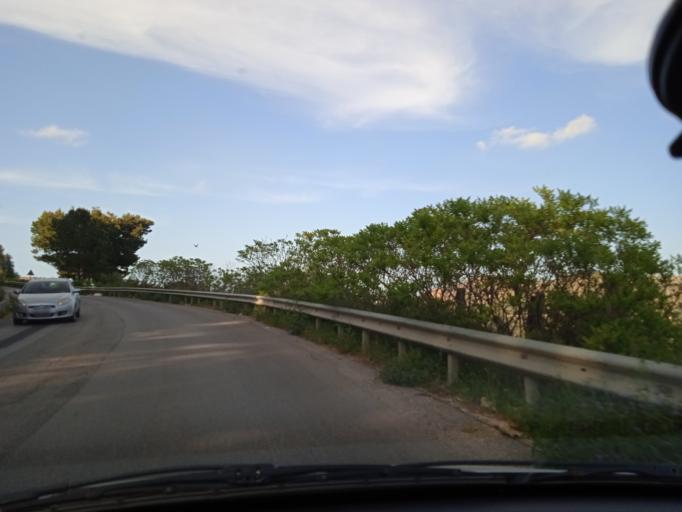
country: IT
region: Sicily
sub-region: Palermo
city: Portella di Mare
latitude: 38.0575
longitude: 13.4615
